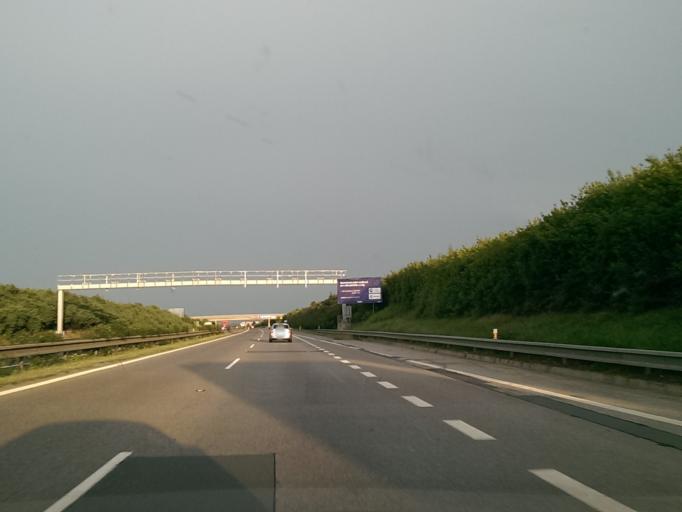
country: CZ
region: Central Bohemia
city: Zdiby
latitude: 50.1677
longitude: 14.4640
